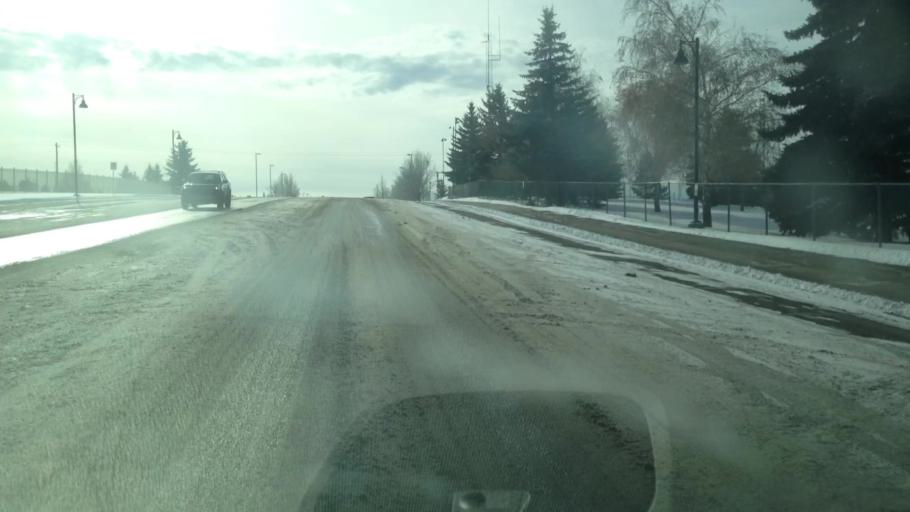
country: US
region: Idaho
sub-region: Madison County
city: Rexburg
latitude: 43.8130
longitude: -111.7838
